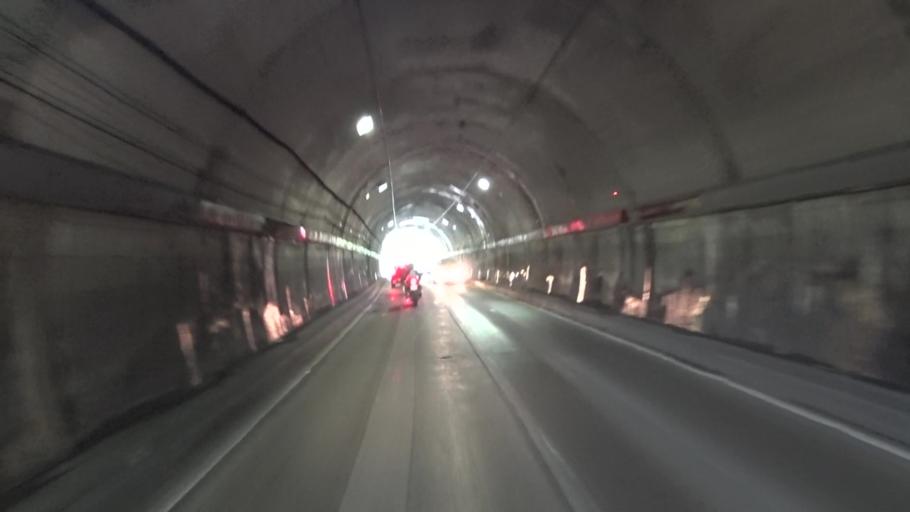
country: JP
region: Shiga Prefecture
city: Kitahama
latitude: 35.1851
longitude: 135.8578
